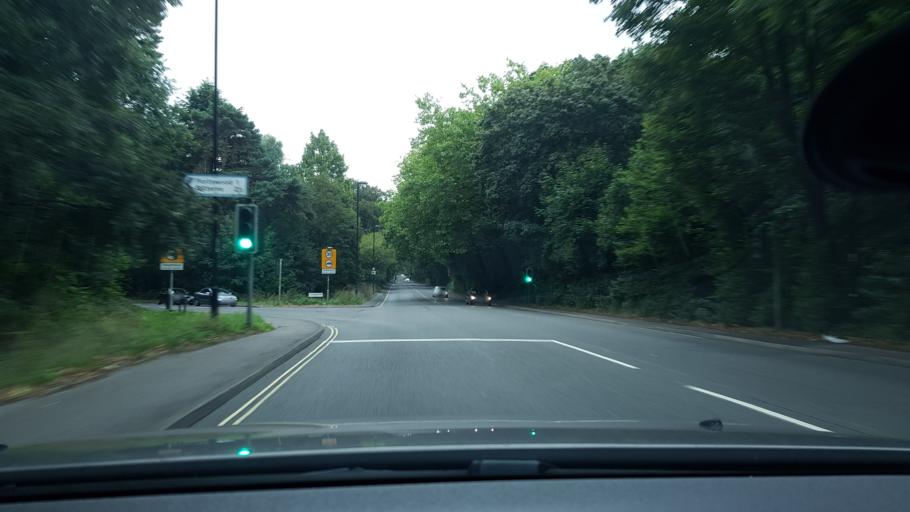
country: GB
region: England
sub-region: Southampton
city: Southampton
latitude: 50.9351
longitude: -1.4063
